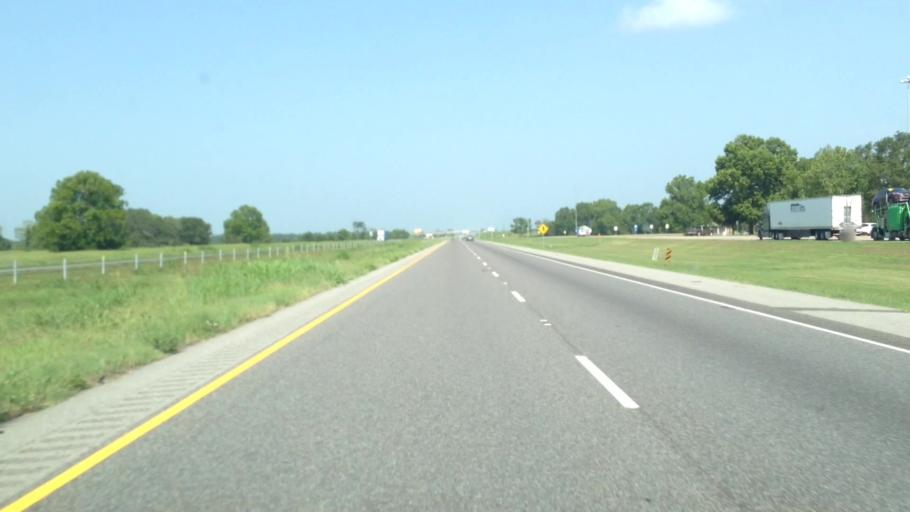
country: US
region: Mississippi
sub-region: Warren County
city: Vicksburg
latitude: 32.3245
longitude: -90.9889
